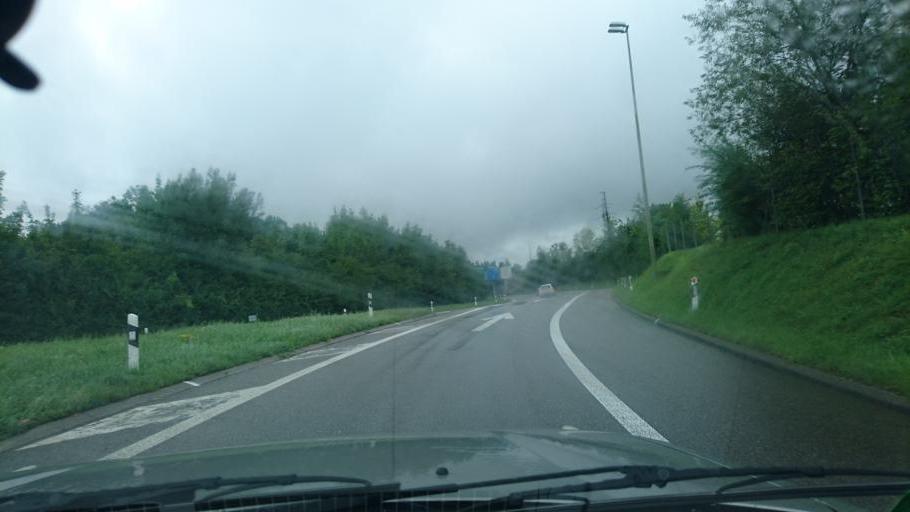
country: CH
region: Zurich
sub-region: Bezirk Hinwil
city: Bubikon
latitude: 47.2868
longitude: 8.8206
